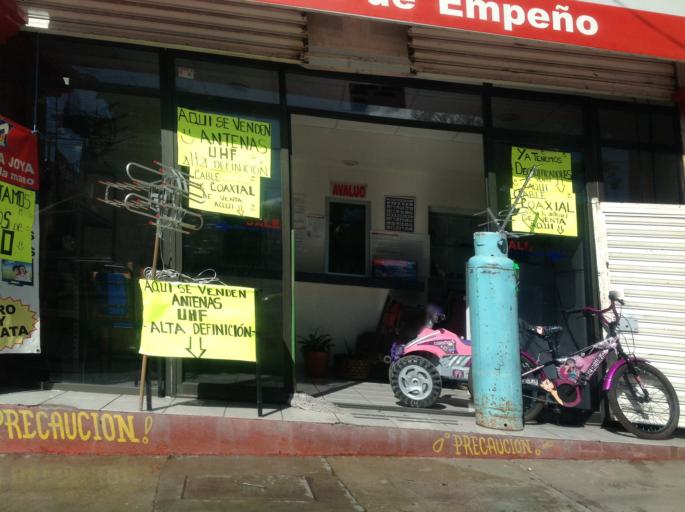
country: MX
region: Oaxaca
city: Ciudad de Huajuapam de Leon
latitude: 17.8111
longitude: -97.7743
